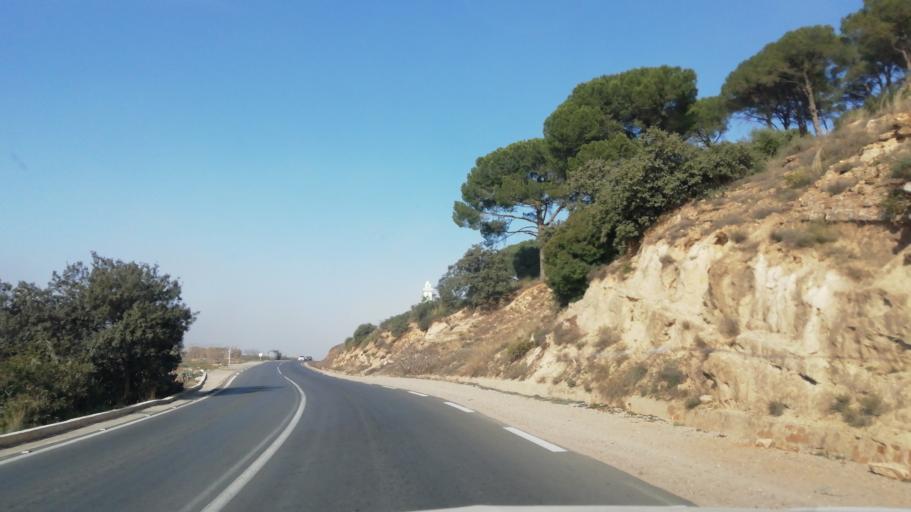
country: DZ
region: Mascara
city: Mascara
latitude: 35.5249
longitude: 0.3489
